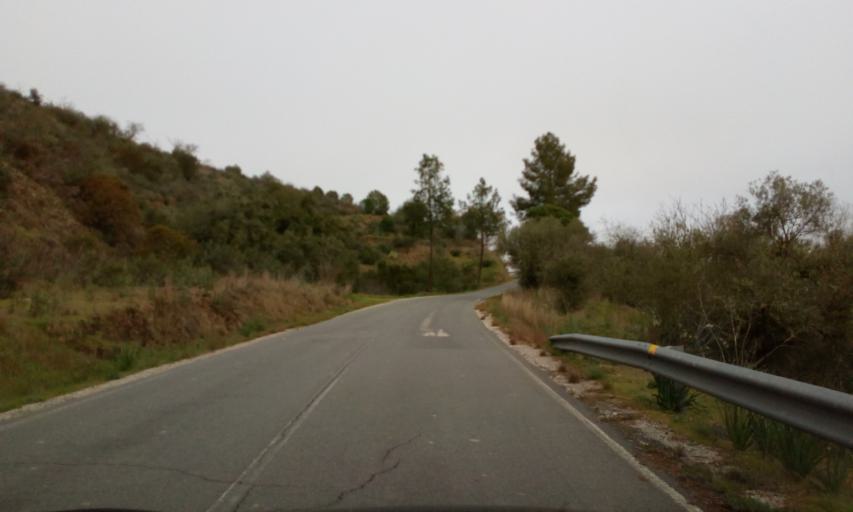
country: ES
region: Andalusia
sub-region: Provincia de Huelva
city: Sanlucar de Guadiana
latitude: 37.4655
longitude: -7.4706
